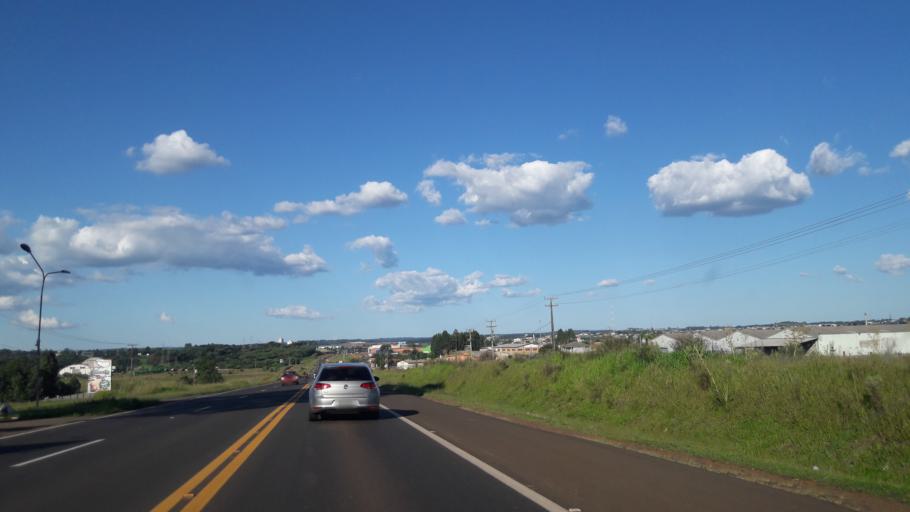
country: BR
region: Parana
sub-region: Guarapuava
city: Guarapuava
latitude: -25.3799
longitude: -51.5084
